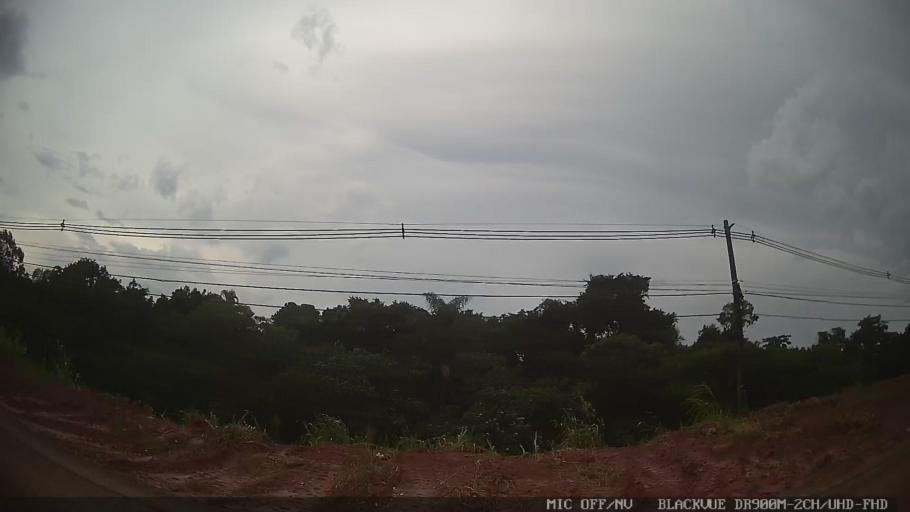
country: BR
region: Sao Paulo
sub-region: Itaquaquecetuba
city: Itaquaquecetuba
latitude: -23.4620
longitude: -46.3024
